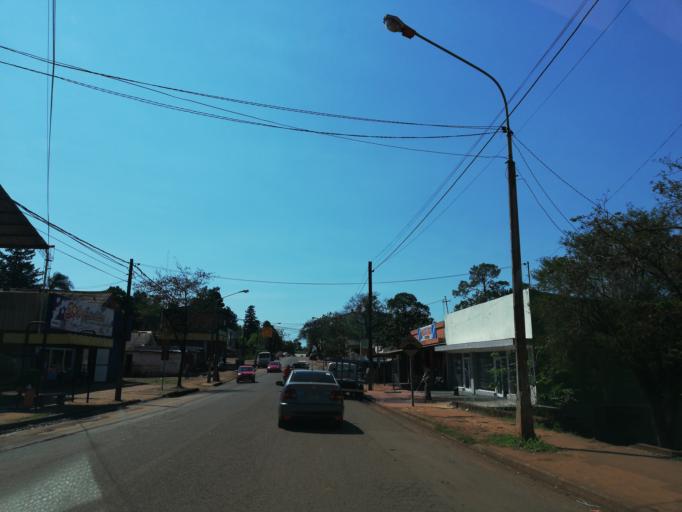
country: AR
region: Misiones
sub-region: Departamento de Eldorado
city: Eldorado
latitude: -26.4040
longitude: -54.6281
